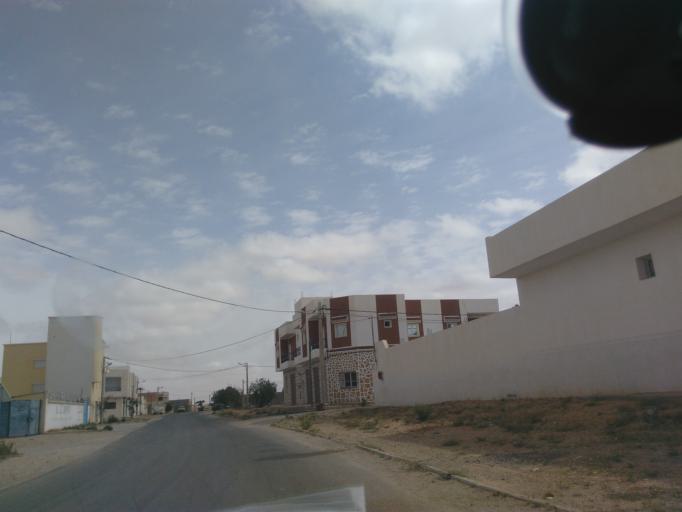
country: TN
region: Tataouine
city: Tataouine
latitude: 32.9539
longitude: 10.4646
